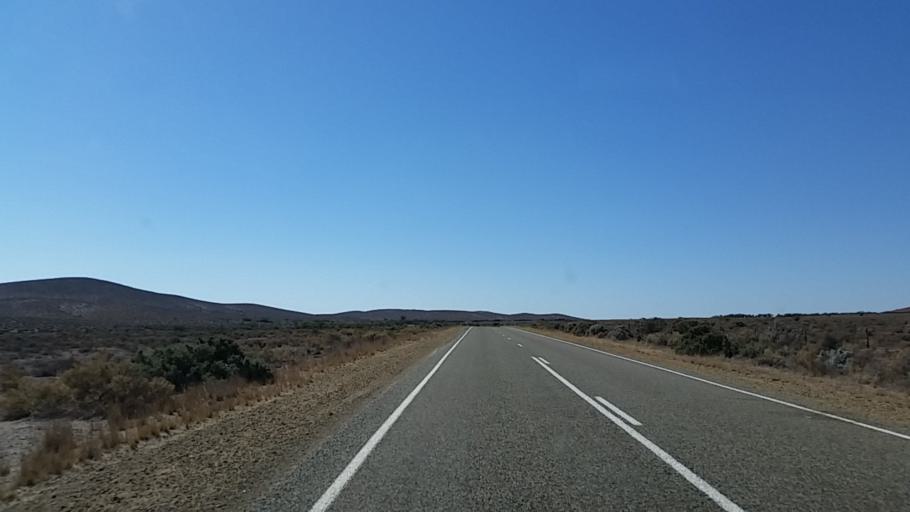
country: AU
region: South Australia
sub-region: Flinders Ranges
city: Quorn
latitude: -32.2222
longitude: 138.5179
